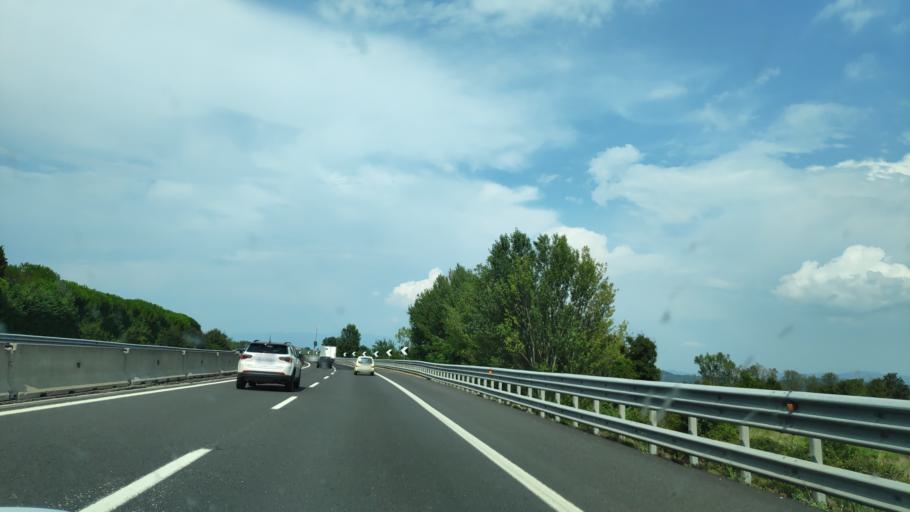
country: IT
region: Tuscany
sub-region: Province of Arezzo
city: Viciomaggio
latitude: 43.4239
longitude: 11.7765
